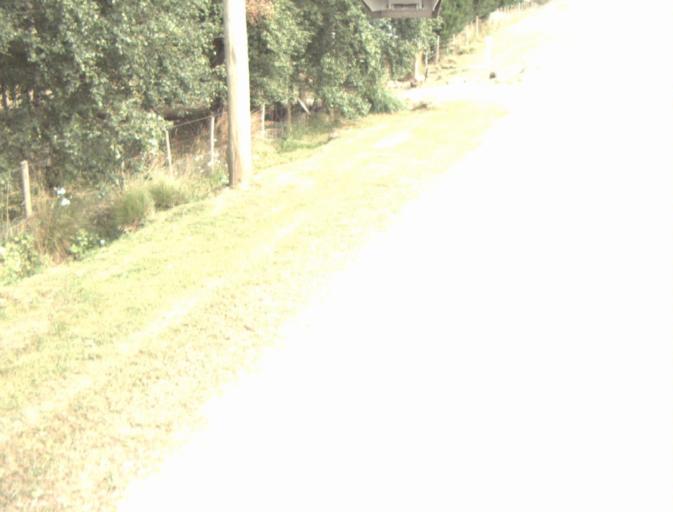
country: AU
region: Tasmania
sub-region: Dorset
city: Scottsdale
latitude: -41.3585
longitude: 147.4606
